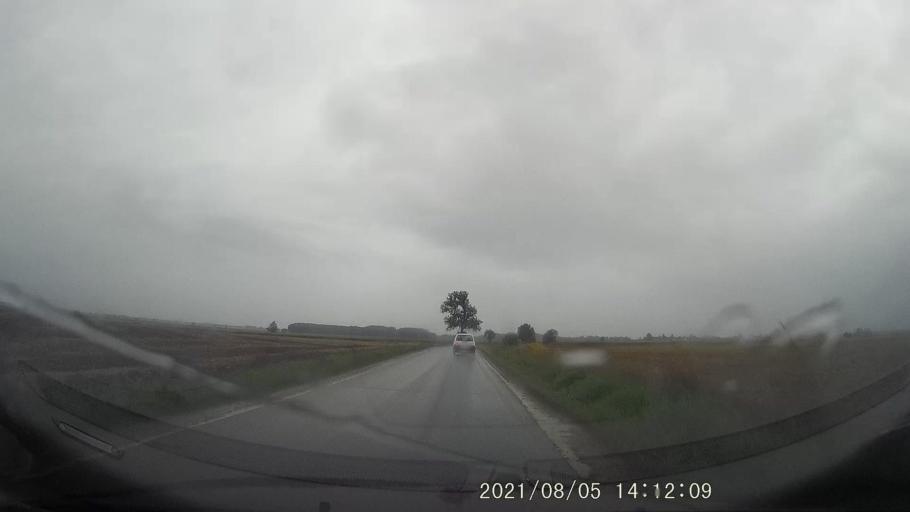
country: PL
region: Opole Voivodeship
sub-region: Powiat krapkowicki
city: Strzeleczki
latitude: 50.4694
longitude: 17.7653
